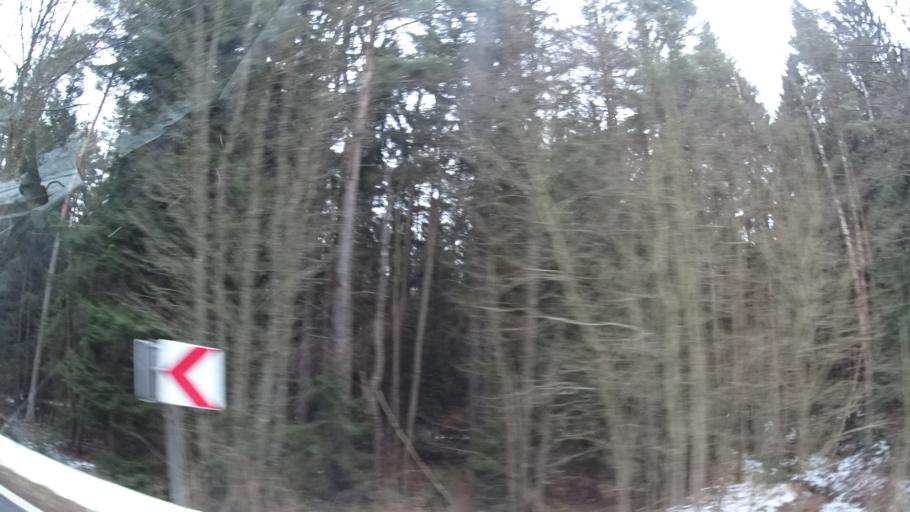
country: DE
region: Thuringia
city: Pennewitz
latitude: 50.6734
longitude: 11.0385
